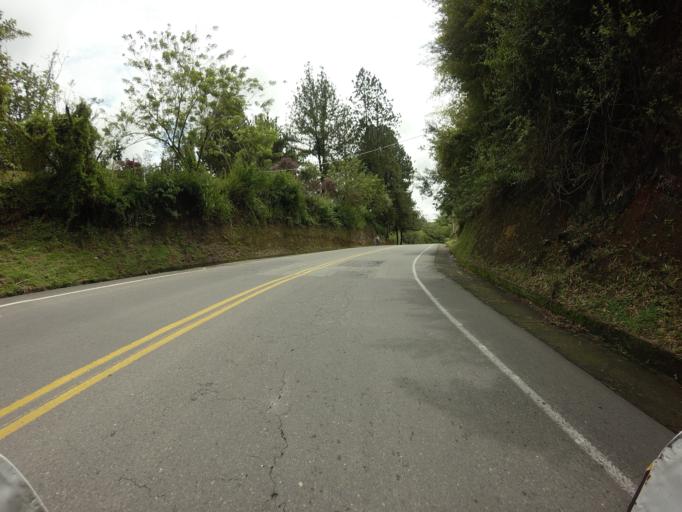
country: CO
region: Quindio
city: Quimbaya
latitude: 4.6433
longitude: -75.7727
